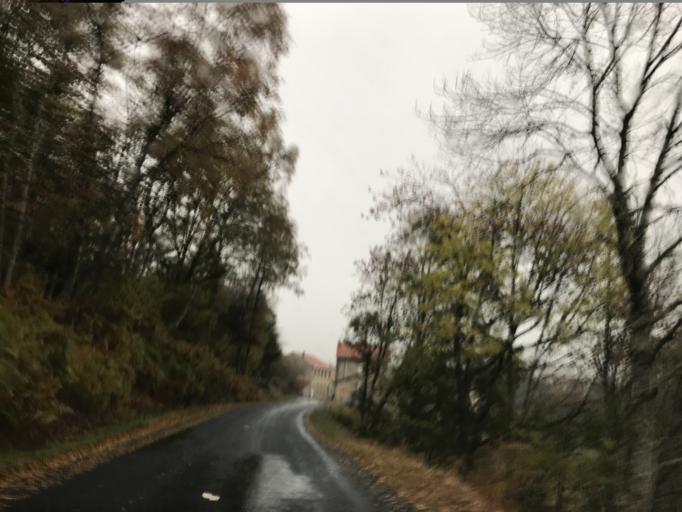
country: FR
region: Auvergne
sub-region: Departement du Puy-de-Dome
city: Celles-sur-Durolle
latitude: 45.7833
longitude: 3.6706
